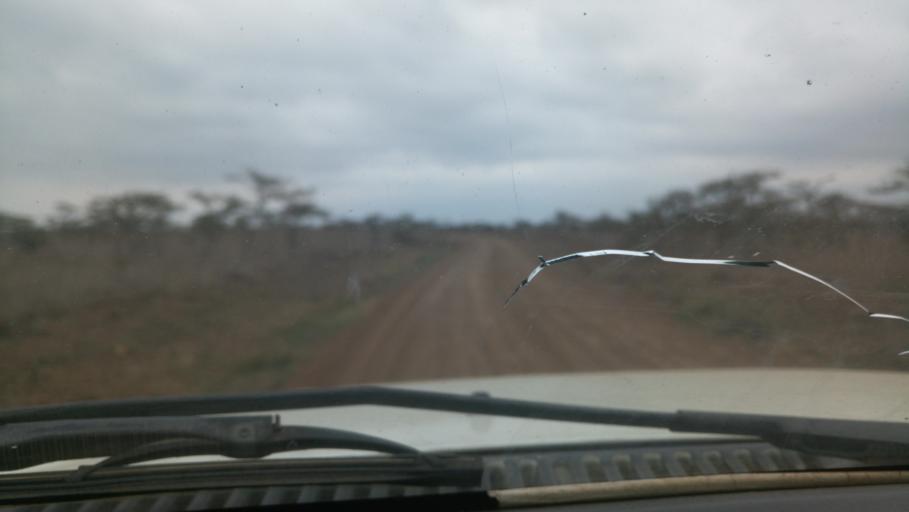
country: KE
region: Nairobi Area
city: Pumwani
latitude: -1.3487
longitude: 36.8613
